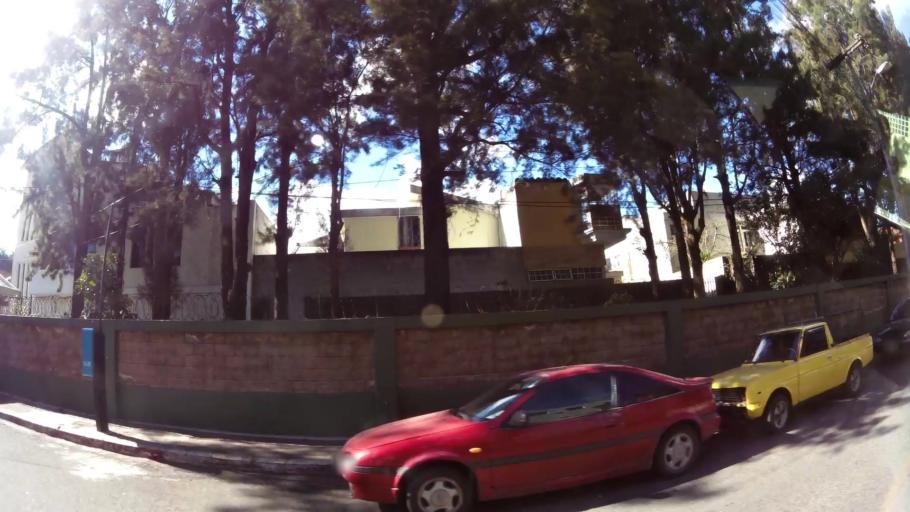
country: GT
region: Guatemala
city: Guatemala City
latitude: 14.6224
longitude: -90.5549
